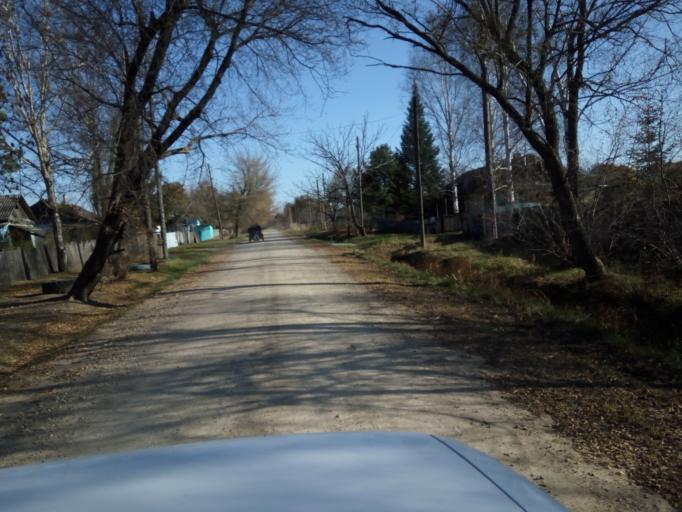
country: RU
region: Primorskiy
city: Lazo
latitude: 45.8722
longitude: 133.6569
